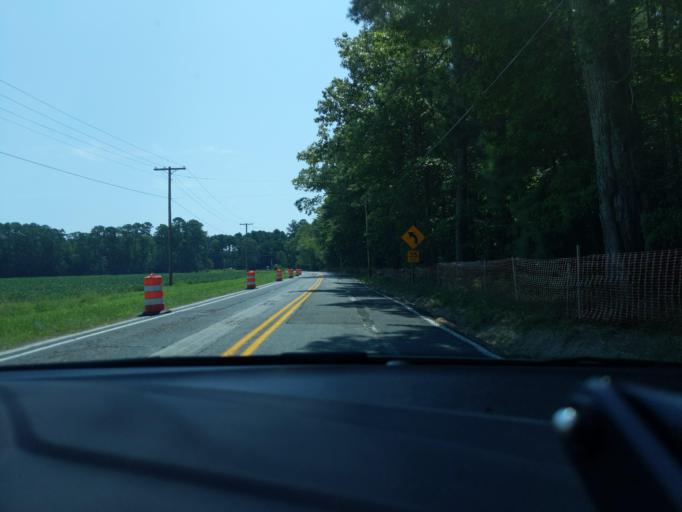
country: US
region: Virginia
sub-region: Northumberland County
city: Heathsville
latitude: 38.0753
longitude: -76.3458
